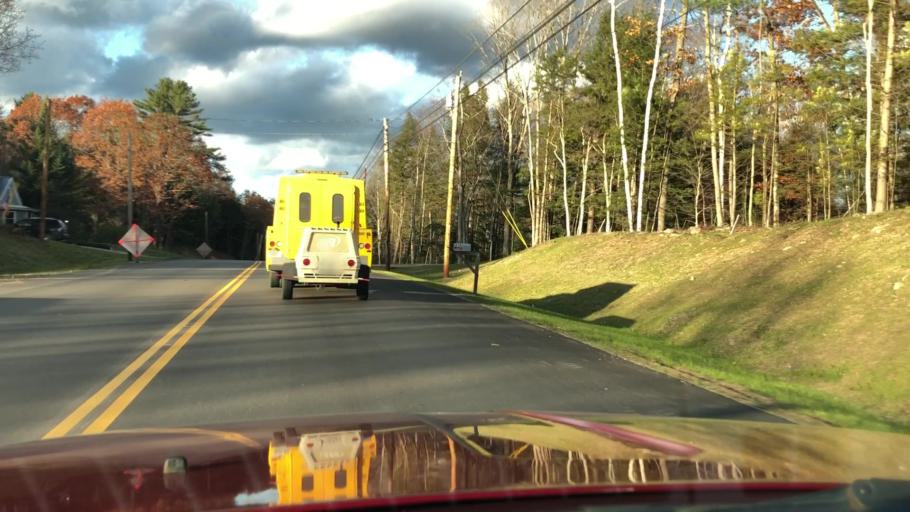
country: US
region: Maine
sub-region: Oxford County
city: Peru
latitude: 44.5221
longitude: -70.4080
